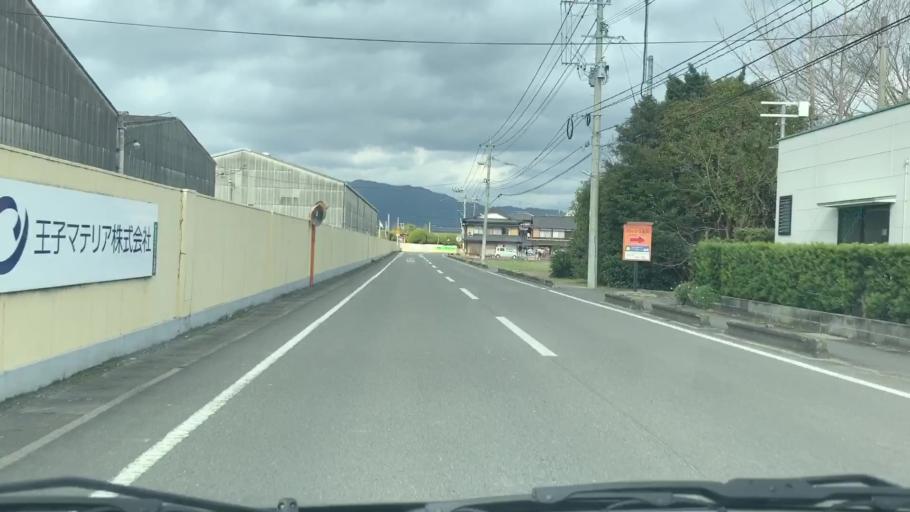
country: JP
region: Saga Prefecture
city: Saga-shi
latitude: 33.2527
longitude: 130.2280
